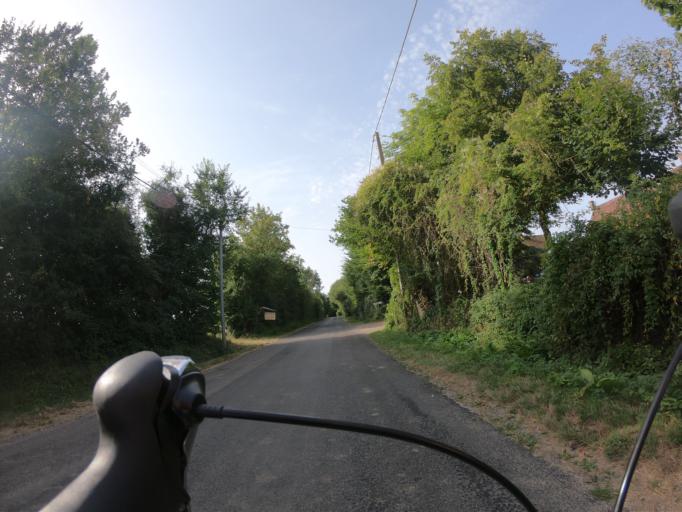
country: FR
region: Lower Normandy
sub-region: Departement de l'Orne
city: Conde-sur-Huisne
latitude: 48.3776
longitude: 0.8315
